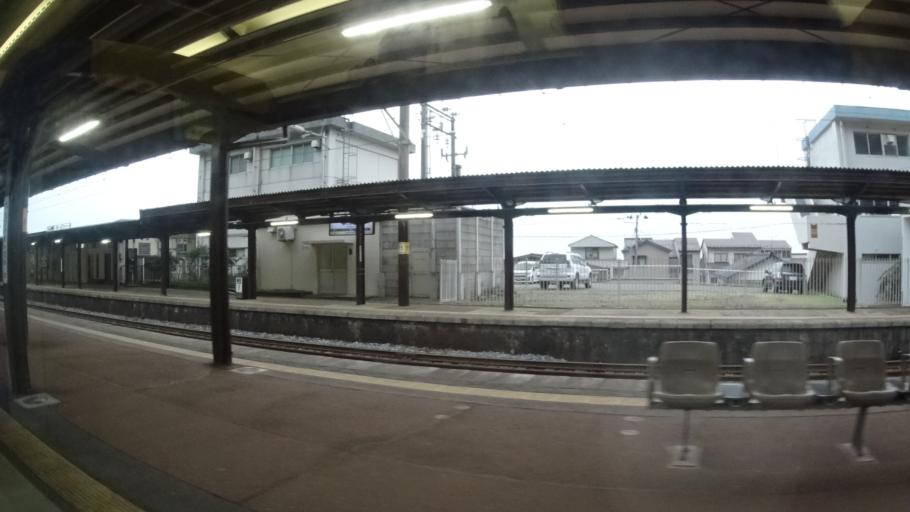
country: JP
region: Yamagata
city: Tsuruoka
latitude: 38.6248
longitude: 139.5883
